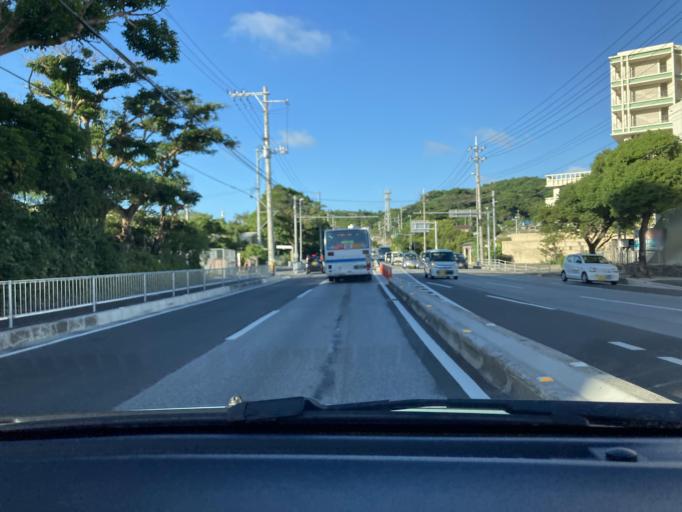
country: JP
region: Okinawa
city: Naha-shi
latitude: 26.2054
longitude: 127.7222
